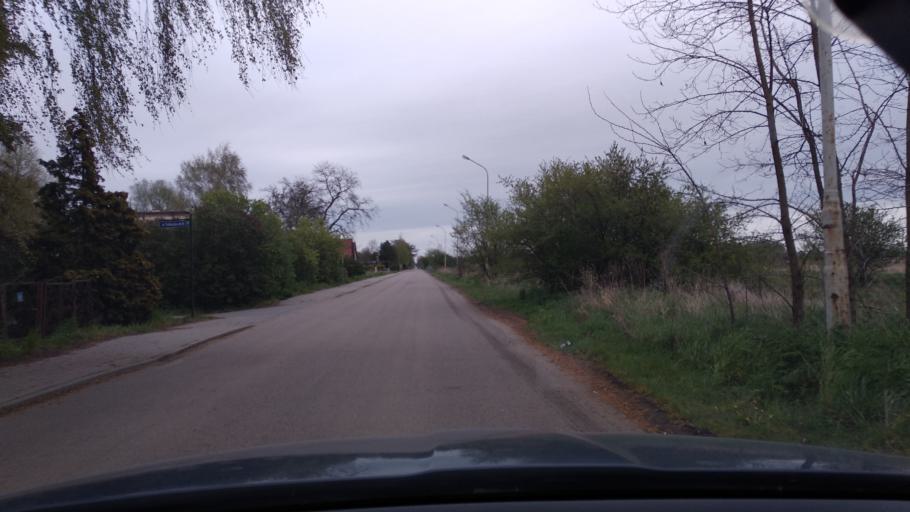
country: PL
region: Pomeranian Voivodeship
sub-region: Powiat gdanski
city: Pruszcz Gdanski
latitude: 54.2773
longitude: 18.6626
